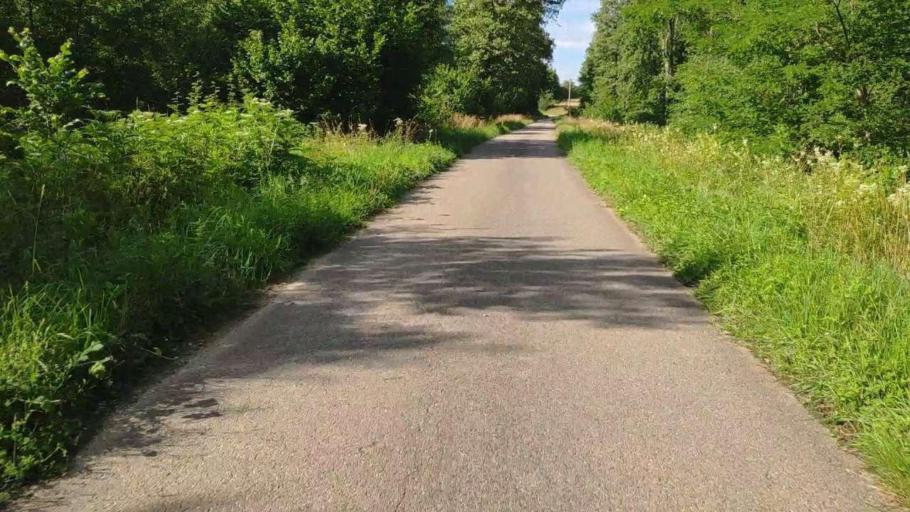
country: FR
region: Franche-Comte
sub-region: Departement du Jura
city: Bletterans
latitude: 46.8166
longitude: 5.4959
